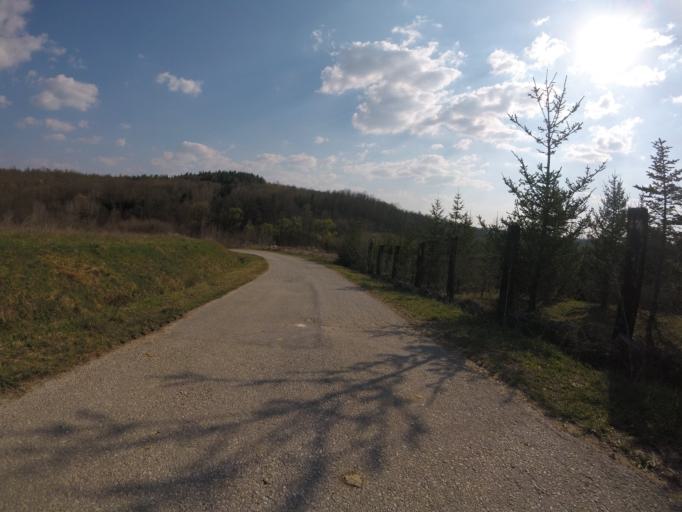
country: HR
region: Sisacko-Moslavacka
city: Glina
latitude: 45.5042
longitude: 16.0063
